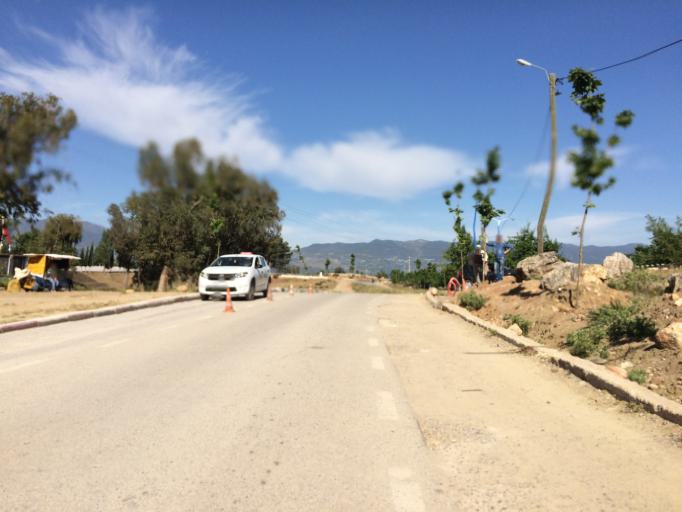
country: MA
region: Tanger-Tetouan
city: Chefchaouene
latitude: 35.1736
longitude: -5.2633
